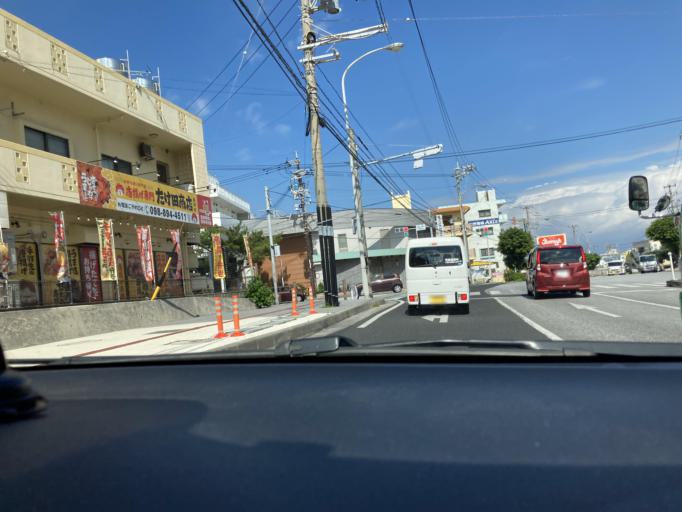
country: JP
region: Okinawa
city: Naha-shi
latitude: 26.2365
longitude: 127.6973
